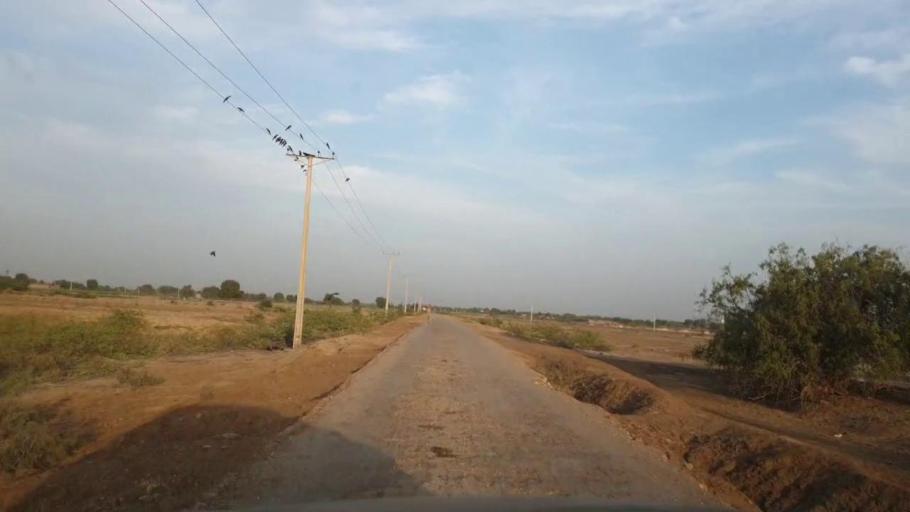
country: PK
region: Sindh
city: Kunri
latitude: 25.1610
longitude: 69.5707
